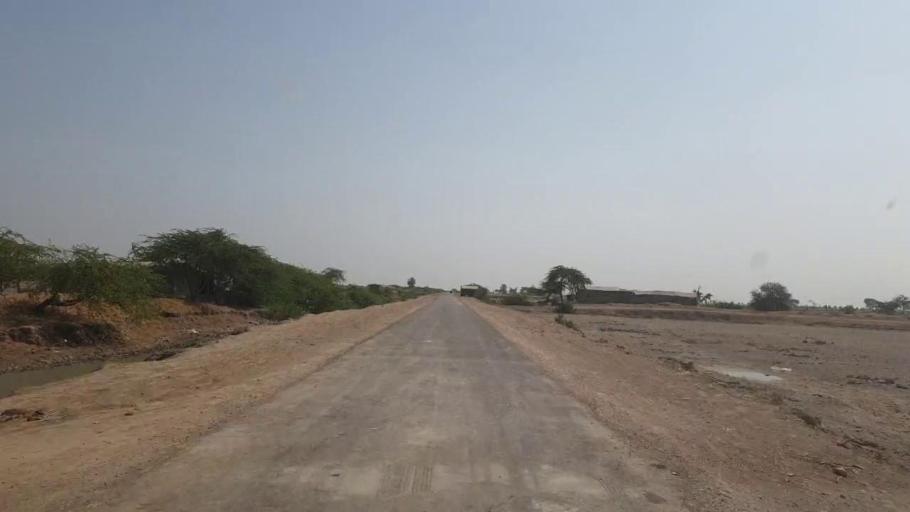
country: PK
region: Sindh
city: Jati
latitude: 24.4601
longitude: 68.5120
